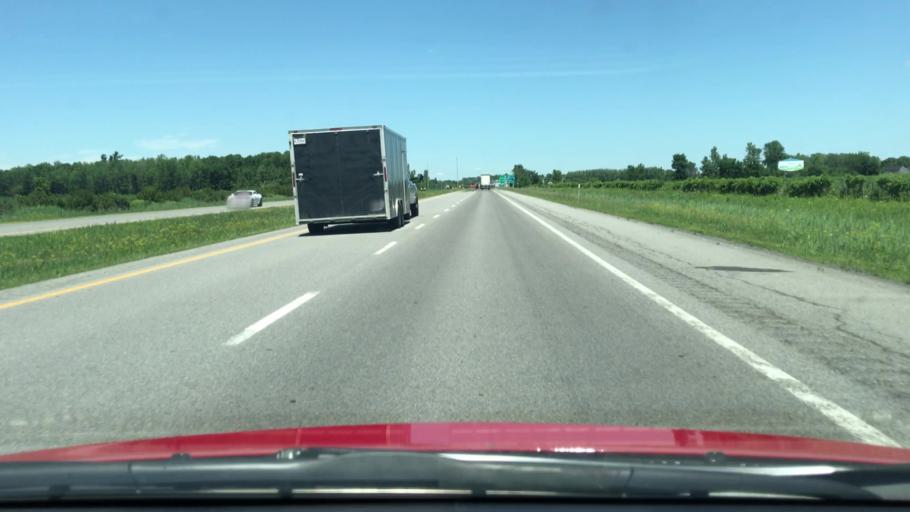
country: CA
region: Quebec
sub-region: Monteregie
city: Napierville
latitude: 45.1820
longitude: -73.4569
